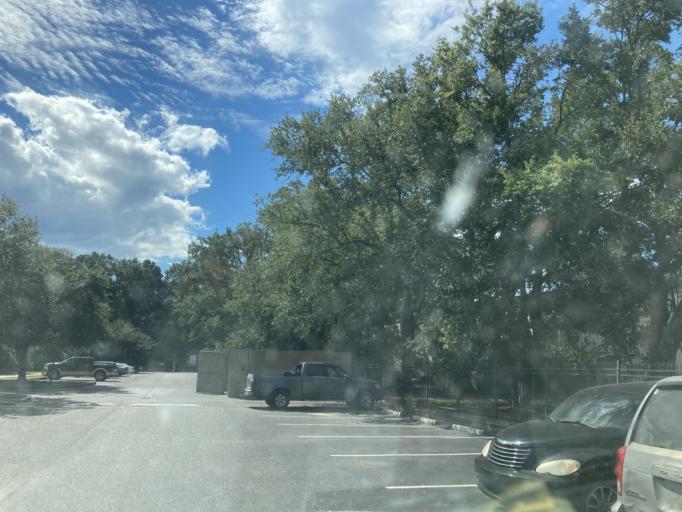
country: US
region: Mississippi
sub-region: Jackson County
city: Saint Martin
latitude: 30.4424
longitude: -88.8577
